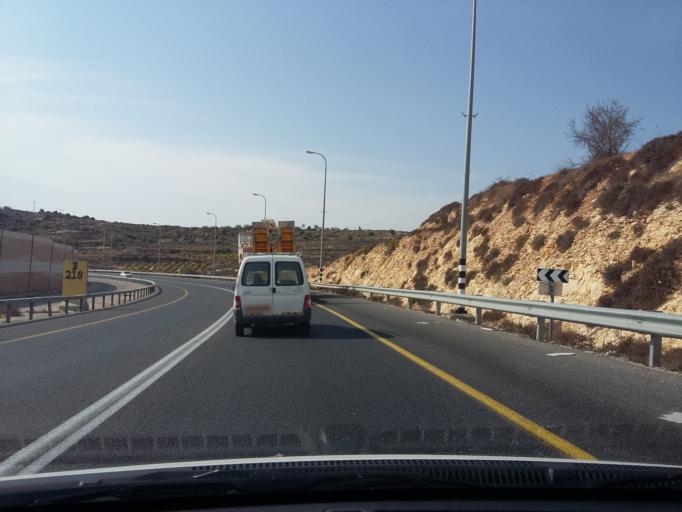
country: PS
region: West Bank
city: Al Khadir
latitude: 31.6968
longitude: 35.1555
